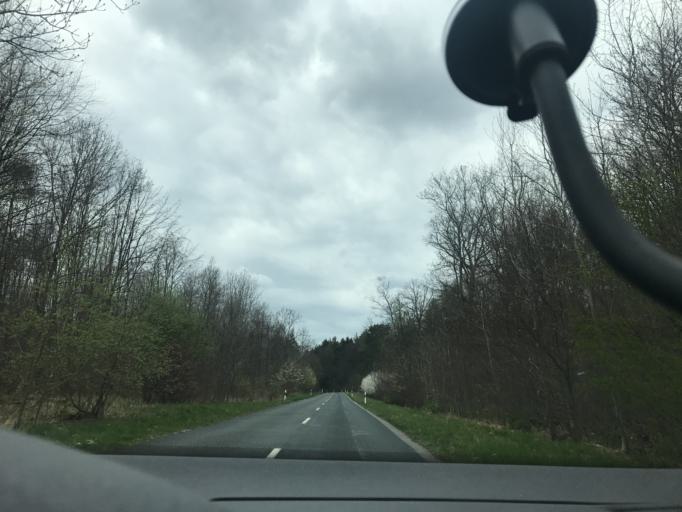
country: DE
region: Lower Saxony
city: Warberg
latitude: 52.1542
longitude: 10.9263
